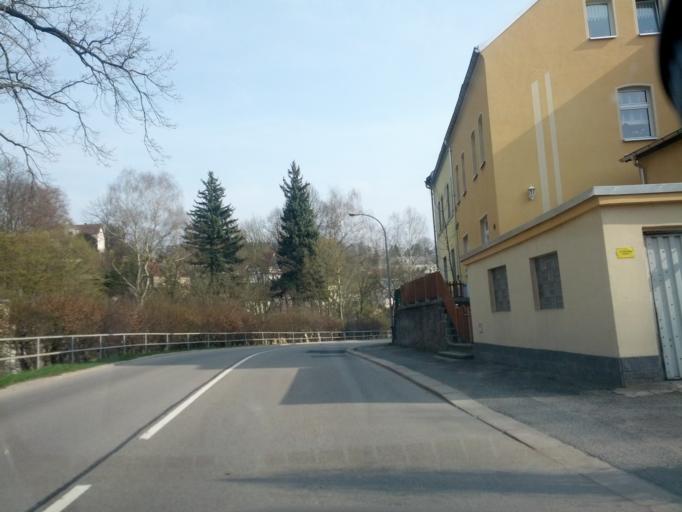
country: DE
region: Saxony
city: Kirchberg
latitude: 50.6214
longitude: 12.5328
